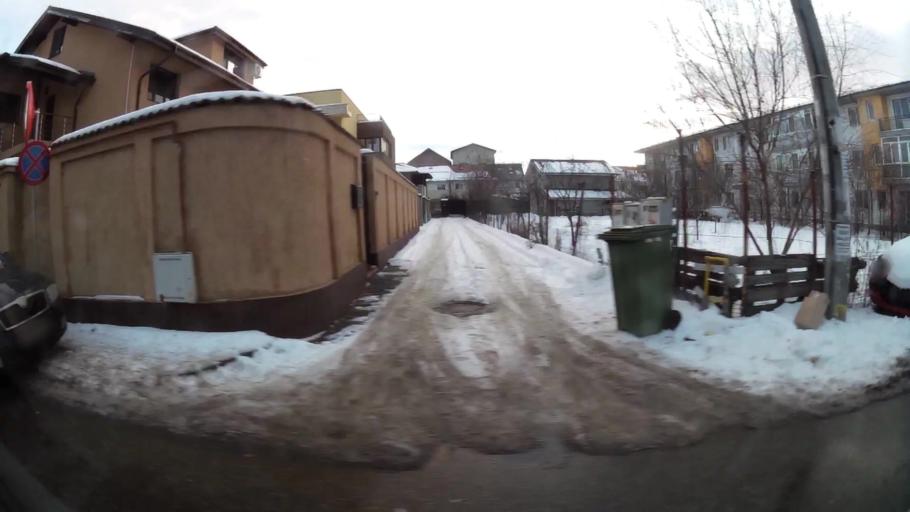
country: RO
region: Ilfov
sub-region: Comuna Popesti-Leordeni
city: Popesti-Leordeni
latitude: 44.3770
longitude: 26.1515
